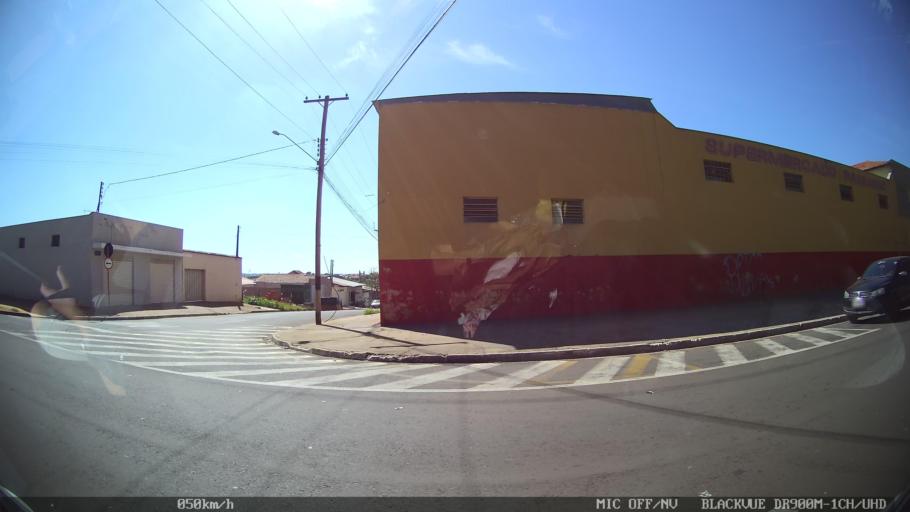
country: BR
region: Sao Paulo
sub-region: Franca
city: Franca
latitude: -20.5440
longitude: -47.4568
